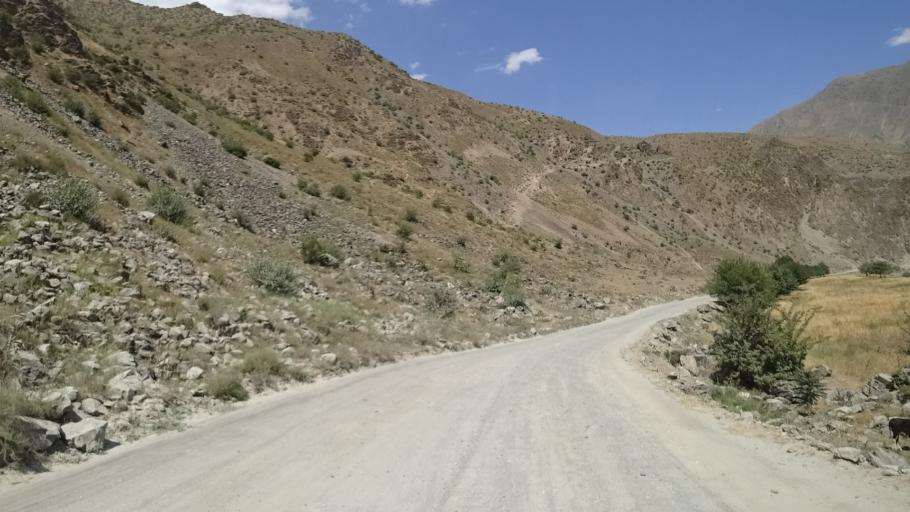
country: AF
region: Badakhshan
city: Maymay
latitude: 38.4430
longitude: 70.9335
